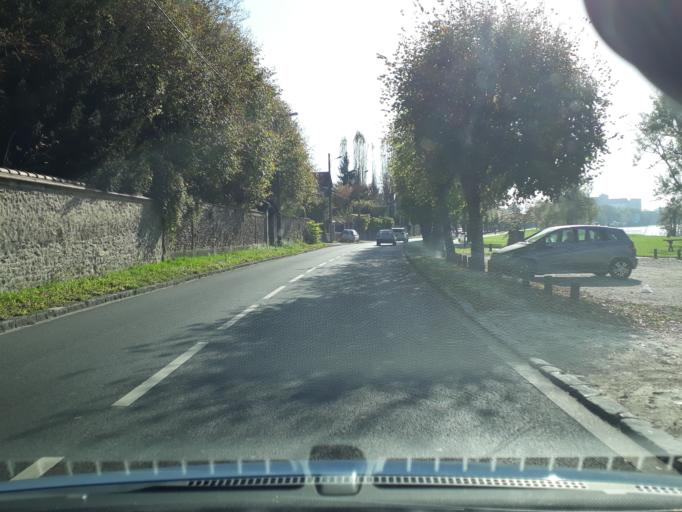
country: FR
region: Ile-de-France
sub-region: Departement de Seine-et-Marne
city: Melun
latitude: 48.5293
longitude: 2.6704
